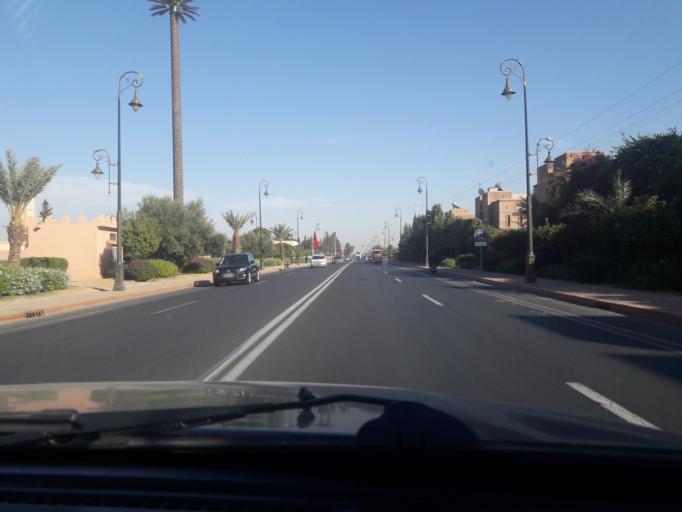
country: MA
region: Marrakech-Tensift-Al Haouz
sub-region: Marrakech
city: Marrakesh
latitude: 31.6482
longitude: -7.9497
